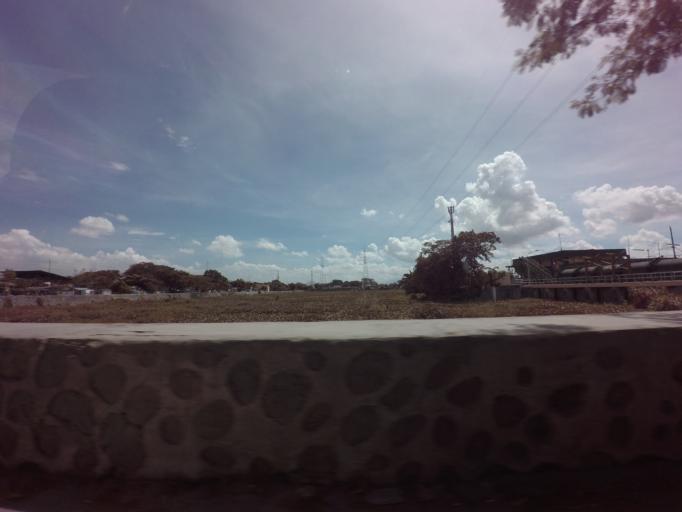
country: PH
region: Calabarzon
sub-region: Province of Rizal
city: Taguig
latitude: 14.5072
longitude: 121.0683
